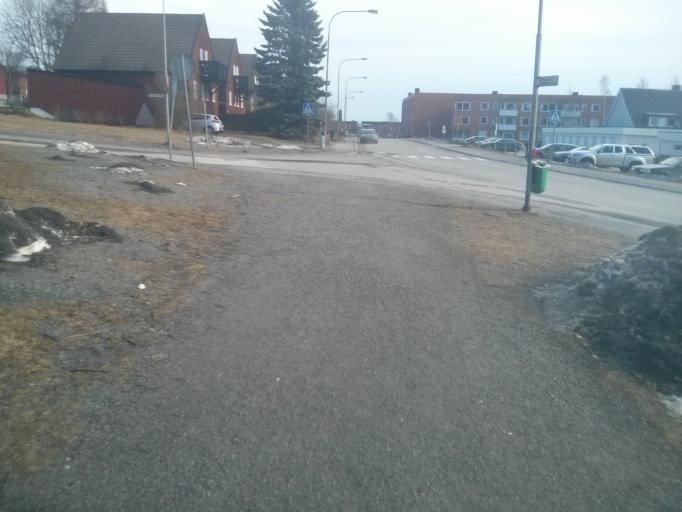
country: SE
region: Vaesternorrland
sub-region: Haernoesands Kommun
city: Haernoesand
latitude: 62.6428
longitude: 17.9243
